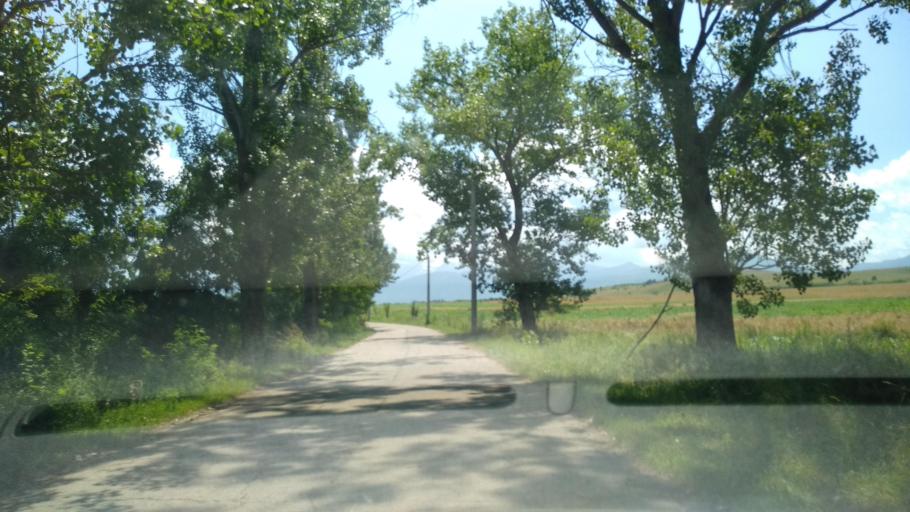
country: RO
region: Hunedoara
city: Densus
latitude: 45.5736
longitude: 22.8093
